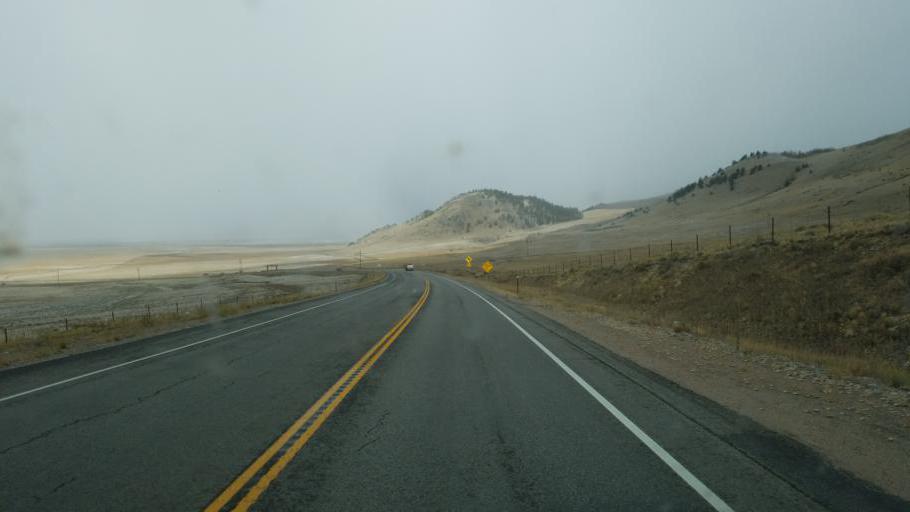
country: US
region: Colorado
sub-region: Summit County
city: Breckenridge
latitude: 39.4051
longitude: -105.7687
